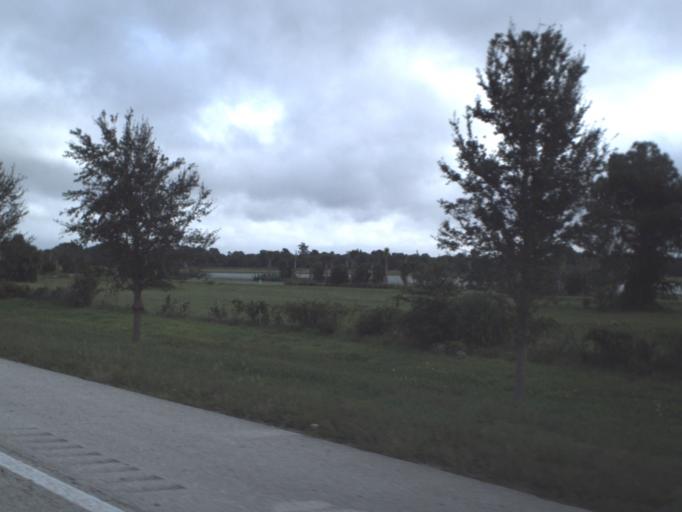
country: US
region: Florida
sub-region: Sarasota County
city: Laurel
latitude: 27.1551
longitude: -82.4597
